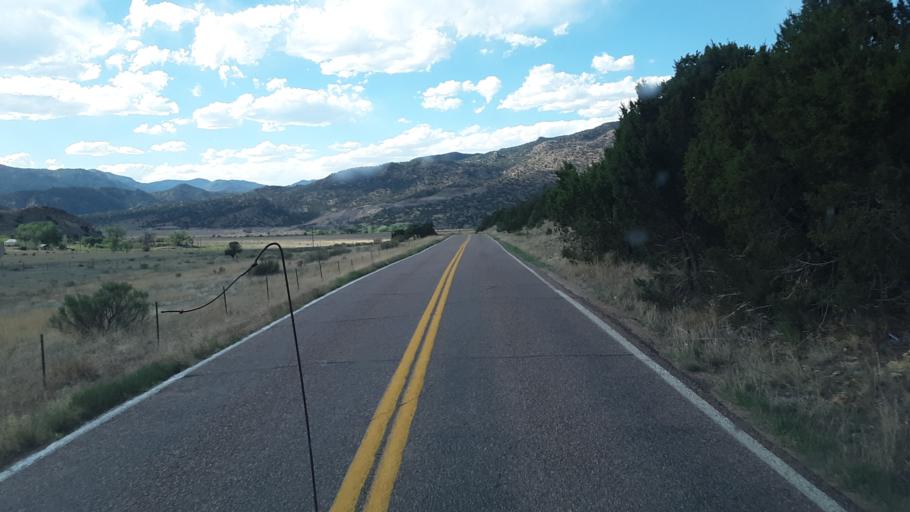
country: US
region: Colorado
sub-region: Fremont County
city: Canon City
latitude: 38.4748
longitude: -105.3784
